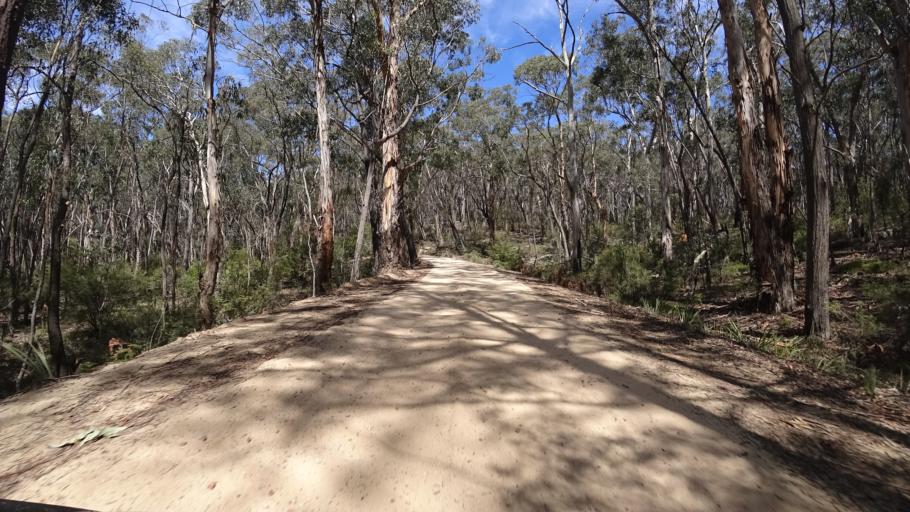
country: AU
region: New South Wales
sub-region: Lithgow
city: Lithgow
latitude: -33.2659
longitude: 150.2243
